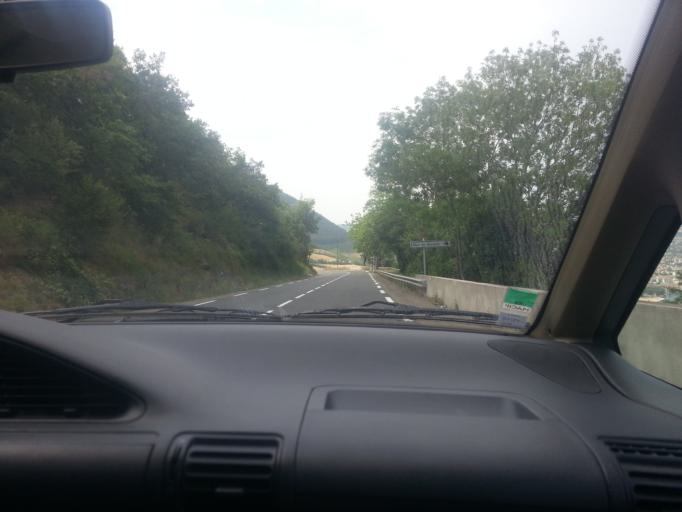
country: FR
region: Midi-Pyrenees
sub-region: Departement de l'Aveyron
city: Millau
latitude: 44.0923
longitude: 3.1031
